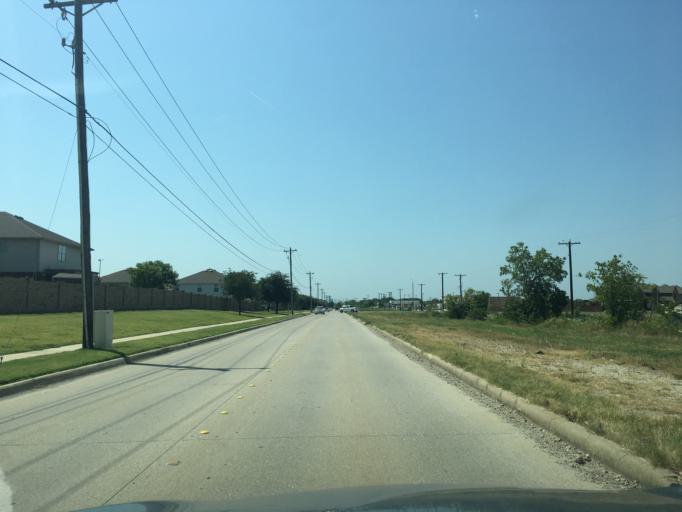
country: US
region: Texas
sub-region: Tarrant County
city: Haslet
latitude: 32.9190
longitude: -97.3315
